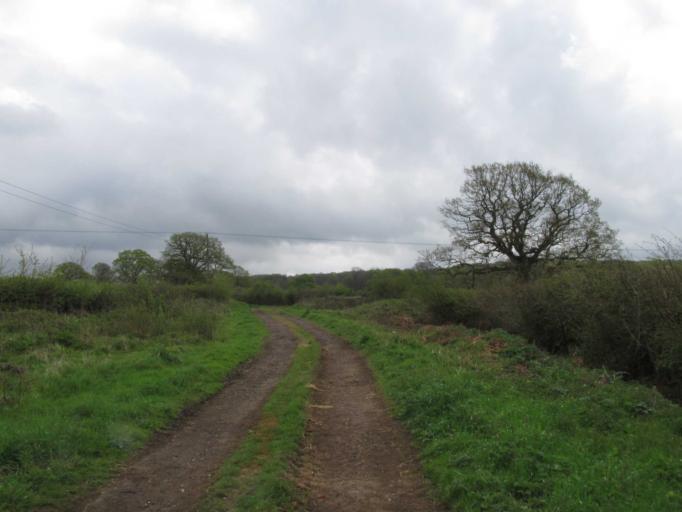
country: GB
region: England
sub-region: Surrey
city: Chiddingfold
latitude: 51.0728
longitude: -0.6421
